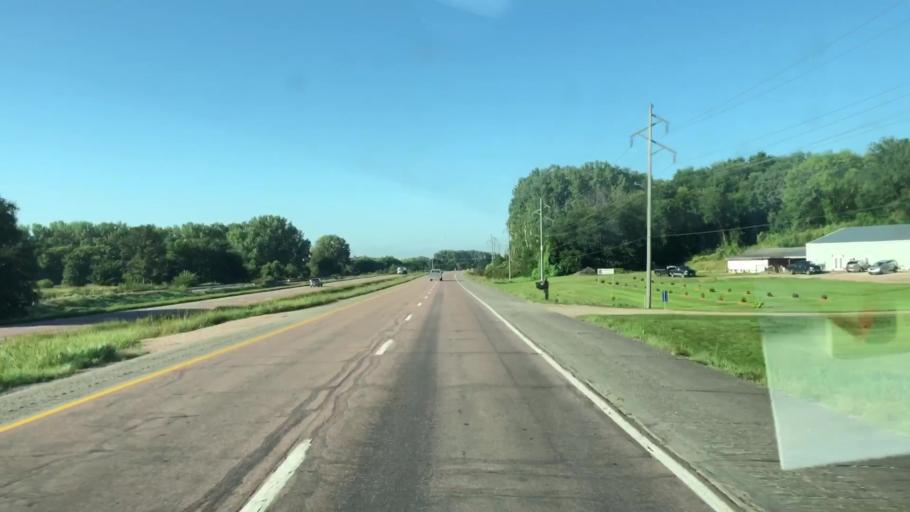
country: US
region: Iowa
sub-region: Woodbury County
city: Sioux City
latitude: 42.5726
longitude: -96.3200
